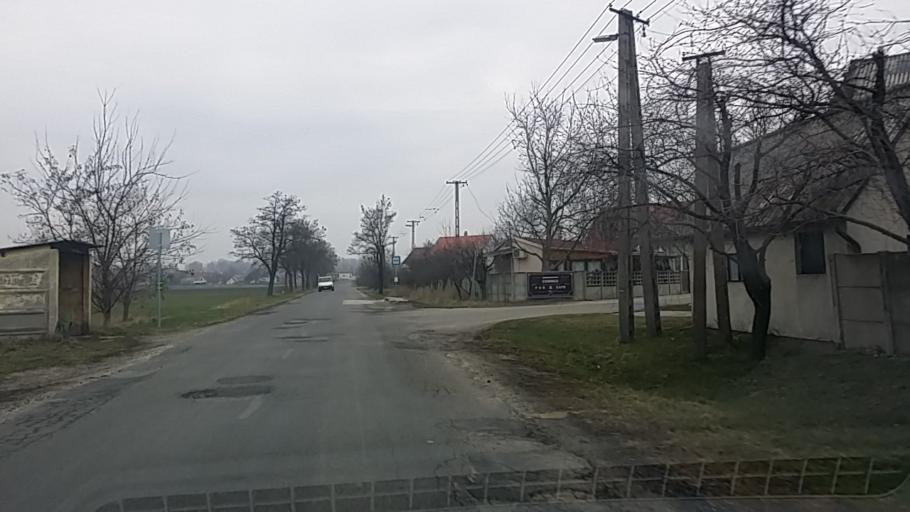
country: HU
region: Komarom-Esztergom
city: Tat
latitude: 47.7411
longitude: 18.6368
